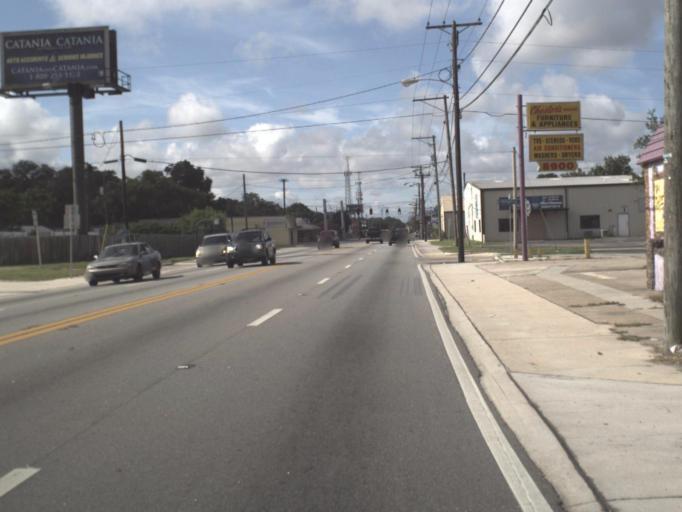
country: US
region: Florida
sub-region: Hillsborough County
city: University
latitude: 28.0312
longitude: -82.4513
